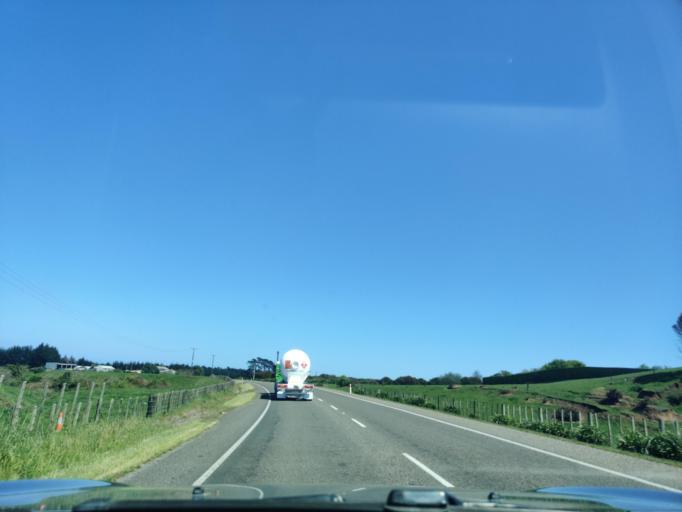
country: NZ
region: Manawatu-Wanganui
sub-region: Wanganui District
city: Wanganui
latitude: -39.8213
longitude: 174.8567
